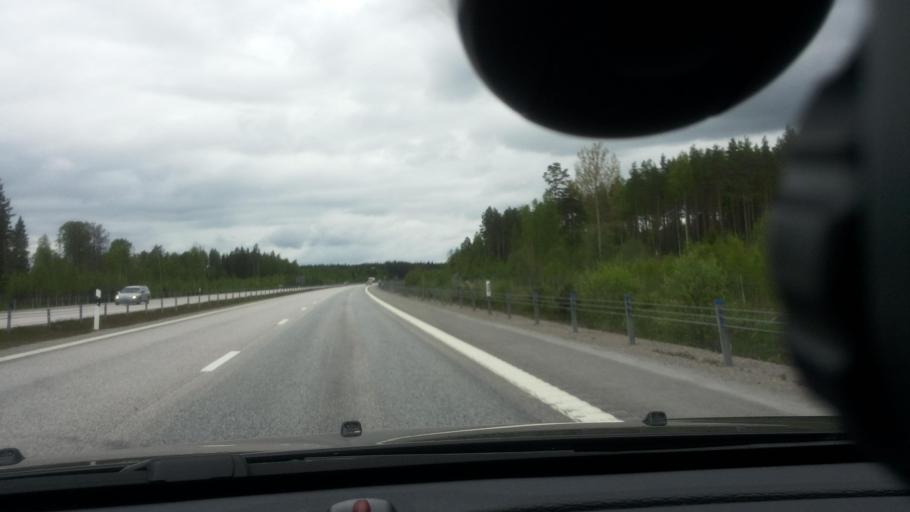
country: SE
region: Uppsala
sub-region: Osthammars Kommun
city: Bjorklinge
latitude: 60.1743
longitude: 17.5135
